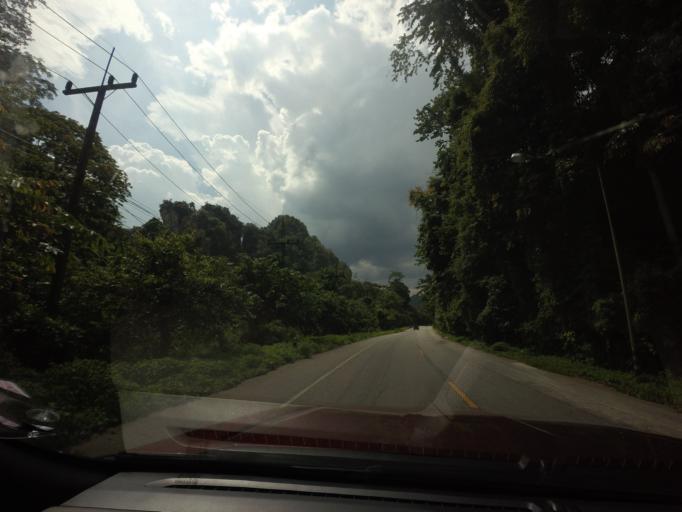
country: TH
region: Yala
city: Than To
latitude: 6.1805
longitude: 101.1741
